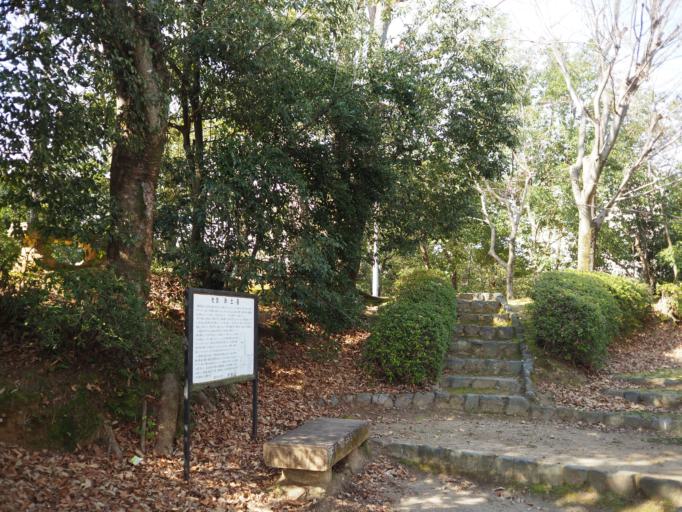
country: JP
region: Kyoto
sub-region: Kyoto-shi
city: Kamigyo-ku
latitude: 35.0459
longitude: 135.7361
